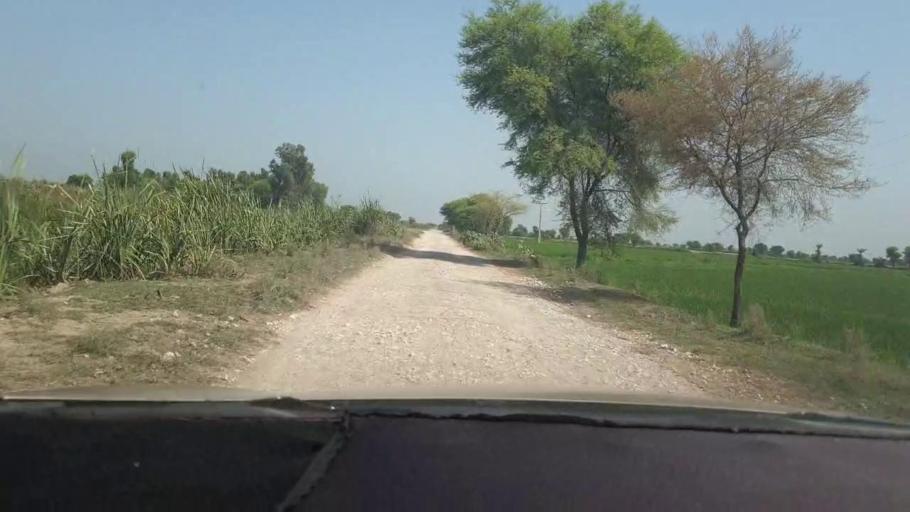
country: PK
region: Sindh
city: Miro Khan
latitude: 27.6726
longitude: 68.1393
